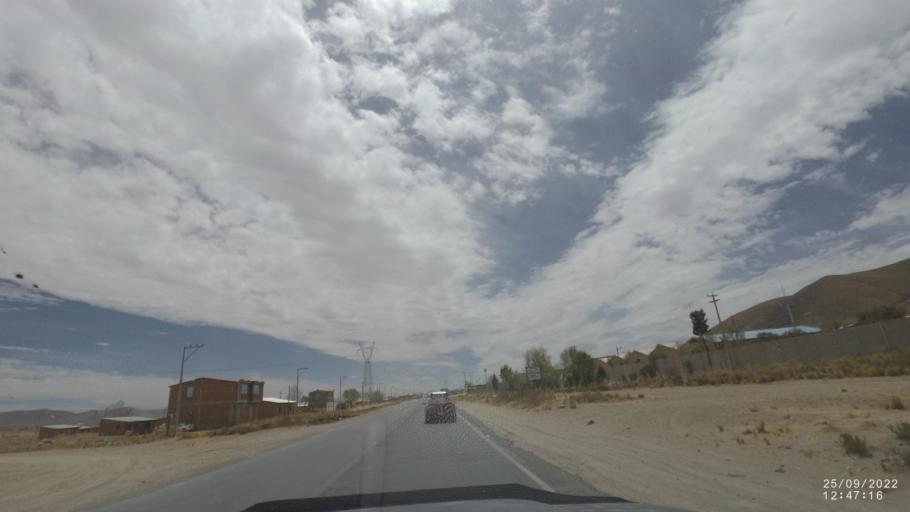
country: BO
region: Oruro
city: Oruro
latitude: -18.0225
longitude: -67.0276
